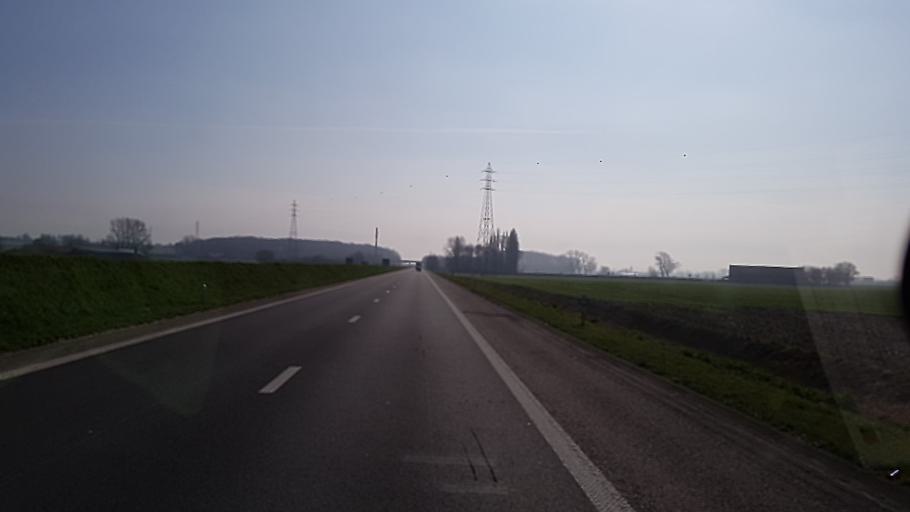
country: BE
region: Flanders
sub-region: Provincie West-Vlaanderen
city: Wervik
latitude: 50.8301
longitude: 3.0366
